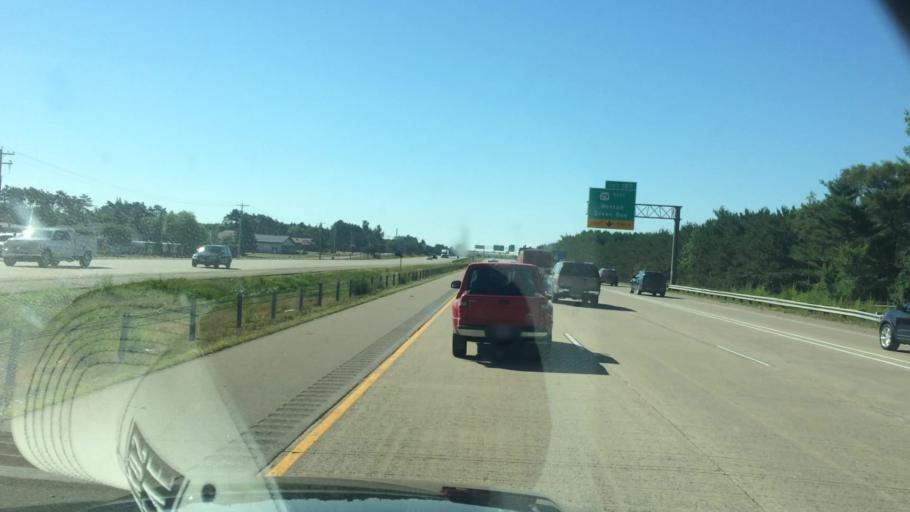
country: US
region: Wisconsin
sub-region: Marathon County
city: Rib Mountain
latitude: 44.9080
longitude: -89.6484
